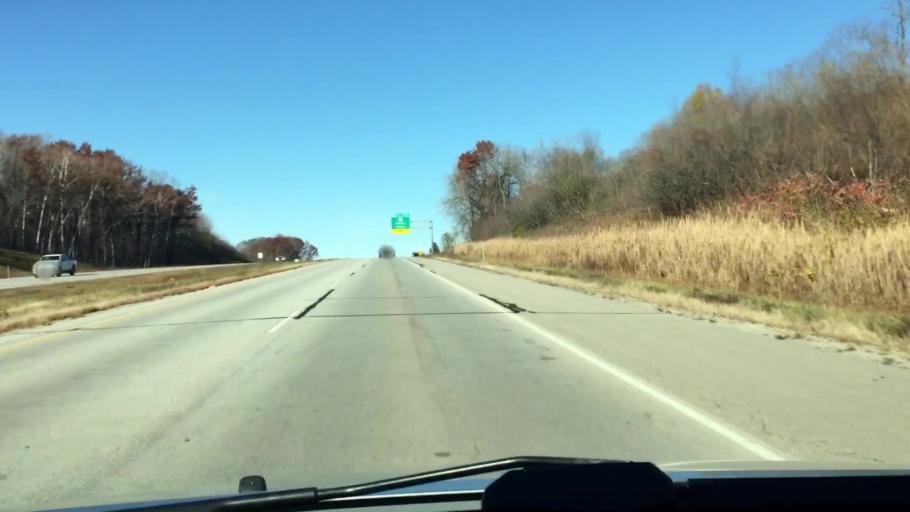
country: US
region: Wisconsin
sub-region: Brown County
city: Howard
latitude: 44.5548
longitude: -88.1163
